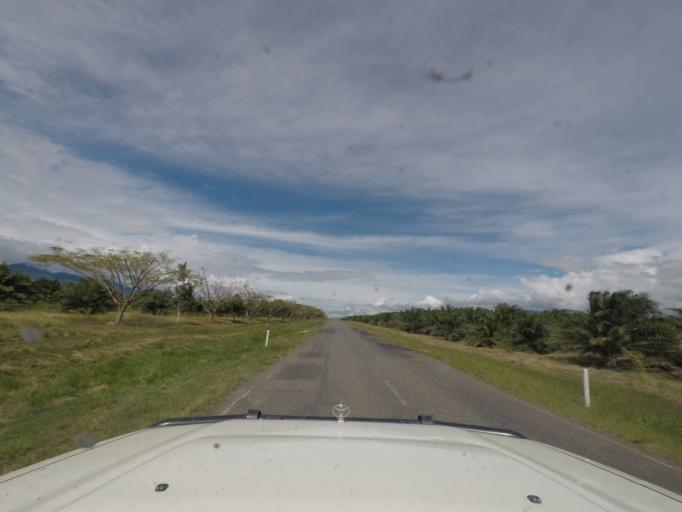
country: PG
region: Eastern Highlands
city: Kainantu
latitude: -6.0445
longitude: 145.9472
